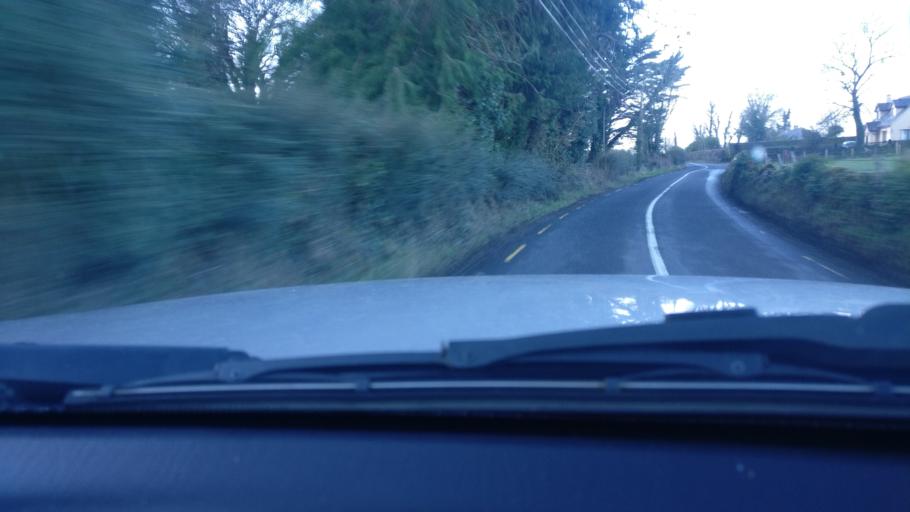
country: IE
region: Connaught
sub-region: County Galway
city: Loughrea
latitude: 53.2271
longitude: -8.4186
